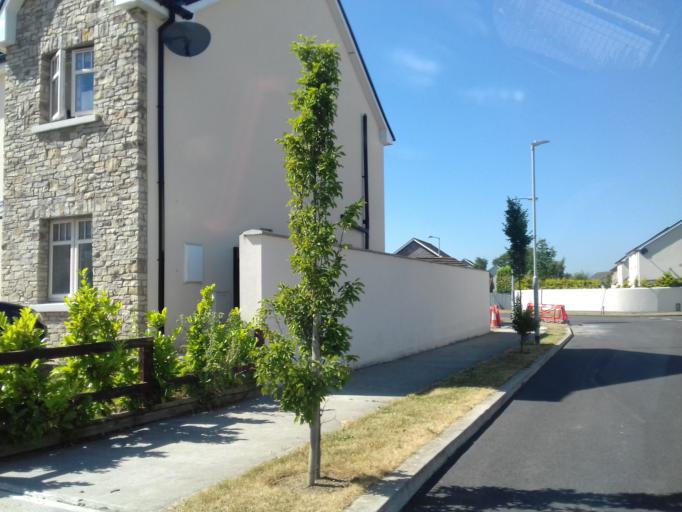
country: IE
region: Leinster
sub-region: Fingal County
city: Swords
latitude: 53.4547
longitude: -6.2581
